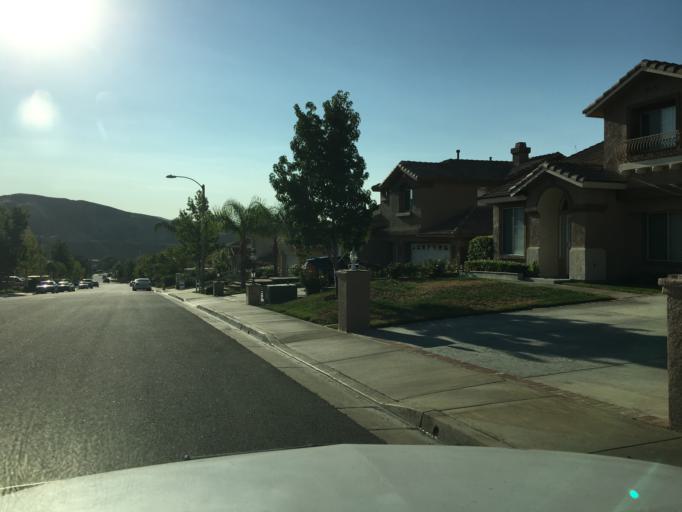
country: US
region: California
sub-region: Los Angeles County
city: Castaic
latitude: 34.5076
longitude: -118.6388
